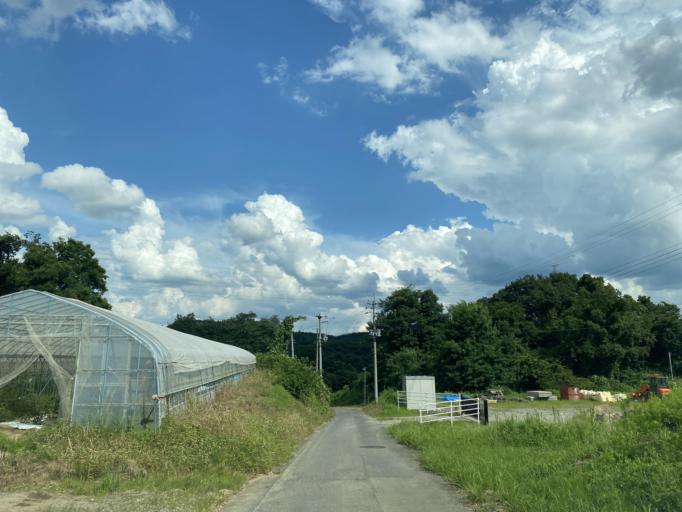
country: JP
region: Fukushima
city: Koriyama
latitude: 37.3779
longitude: 140.4188
